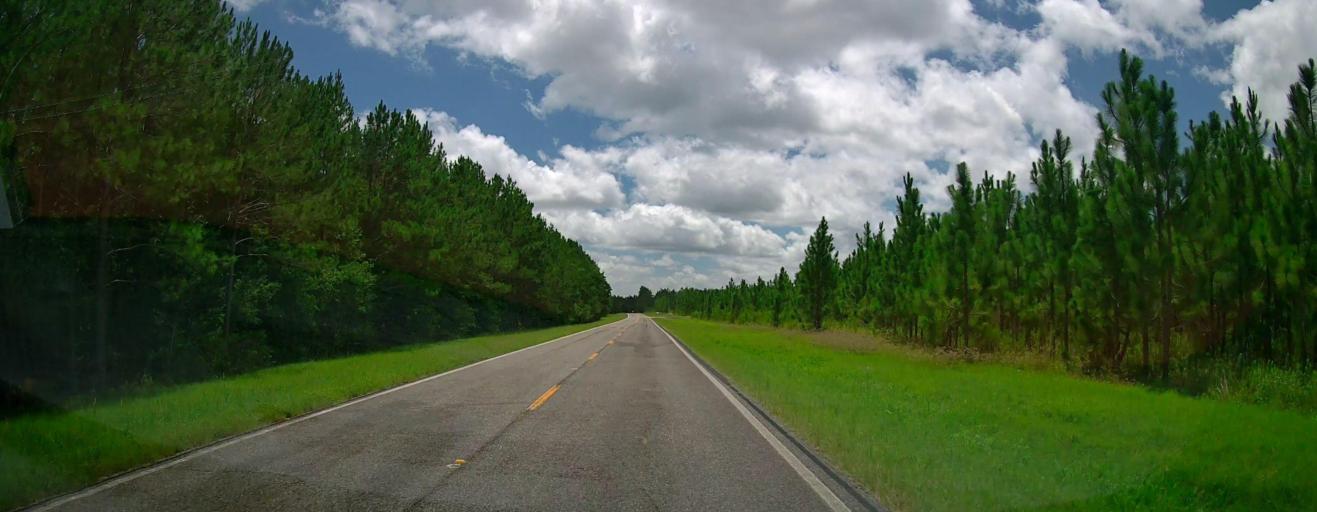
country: US
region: Georgia
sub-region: Wilcox County
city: Rochelle
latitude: 31.8651
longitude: -83.5584
